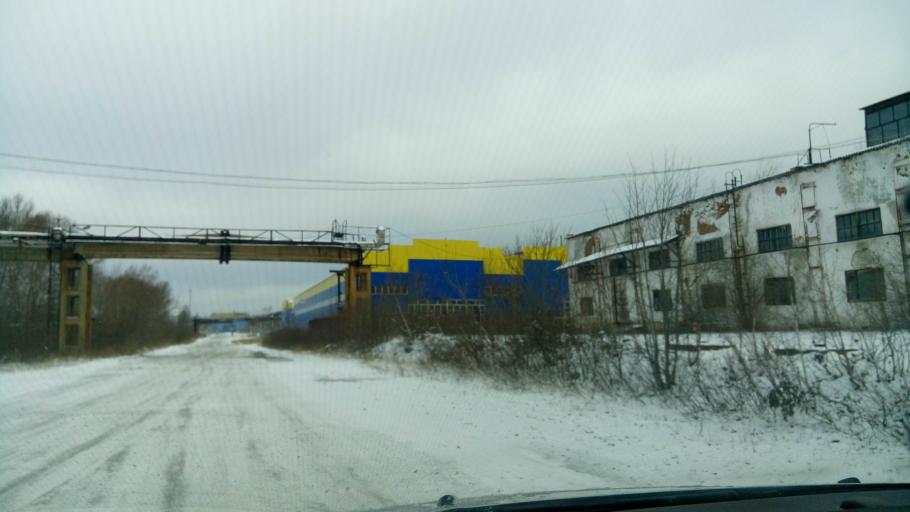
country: RU
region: Sverdlovsk
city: Polevskoy
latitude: 56.4685
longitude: 60.1778
